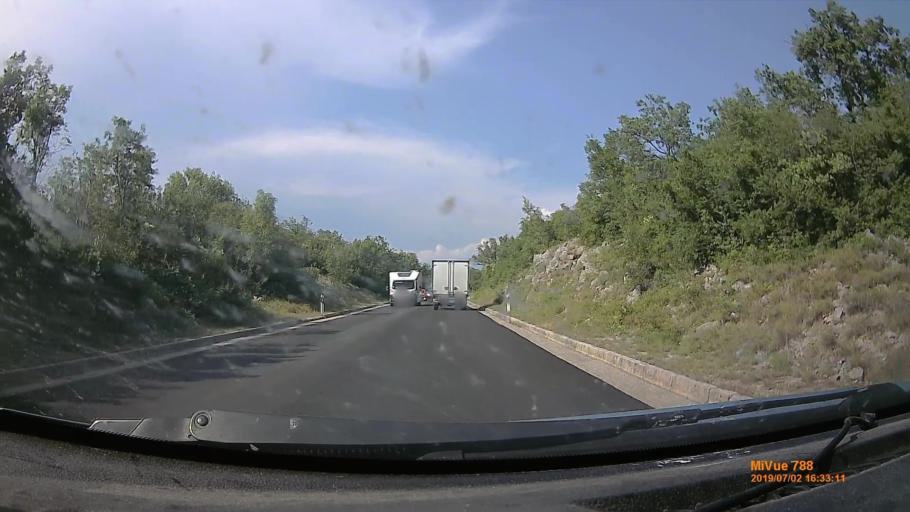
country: HR
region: Primorsko-Goranska
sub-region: Grad Krk
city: Krk
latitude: 45.0721
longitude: 14.4889
